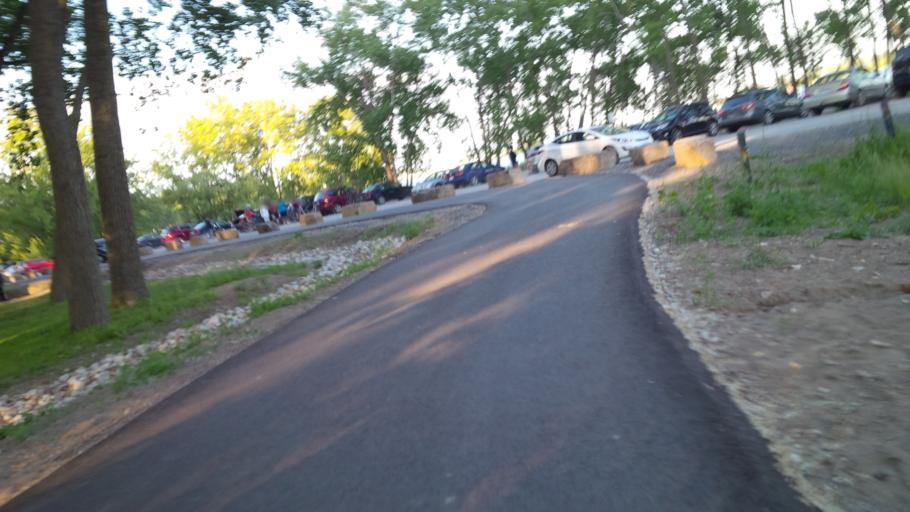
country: CA
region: Ontario
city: Toronto
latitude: 43.6376
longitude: -79.3438
